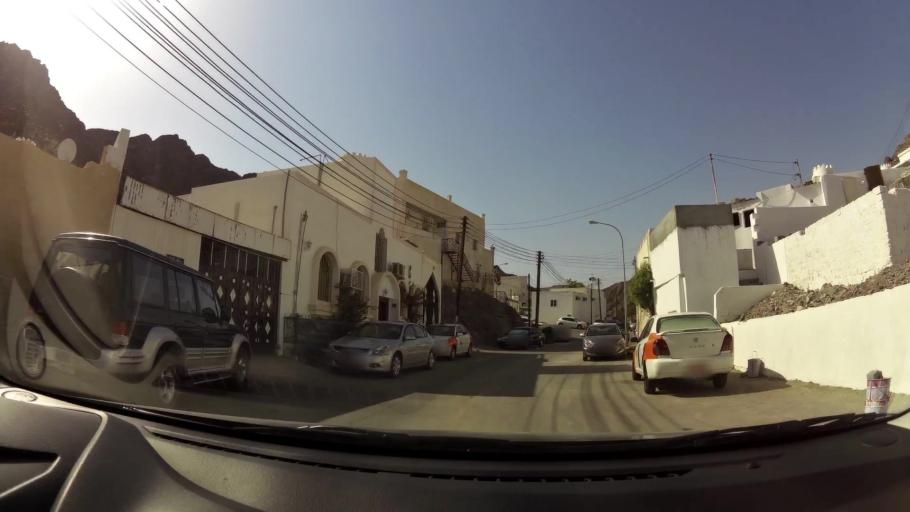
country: OM
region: Muhafazat Masqat
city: Muscat
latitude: 23.6045
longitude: 58.5542
